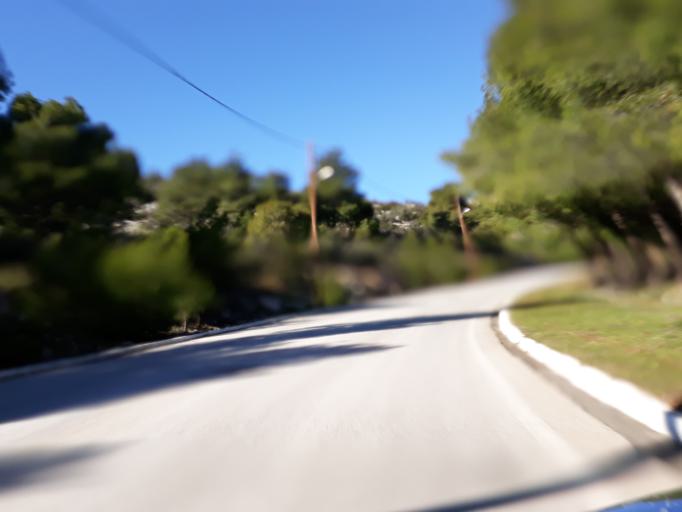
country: GR
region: Attica
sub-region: Nomarchia Dytikis Attikis
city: Fyli
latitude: 38.1045
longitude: 23.6802
